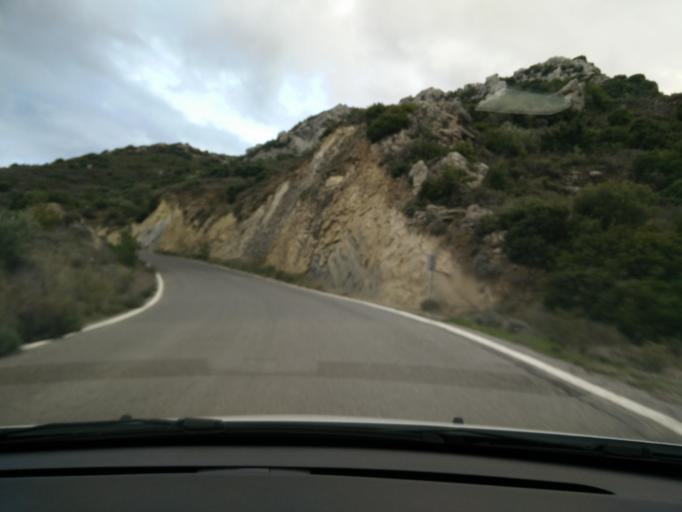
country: GR
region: Crete
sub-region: Nomos Lasithiou
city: Gra Liyia
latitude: 35.0910
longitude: 25.6917
